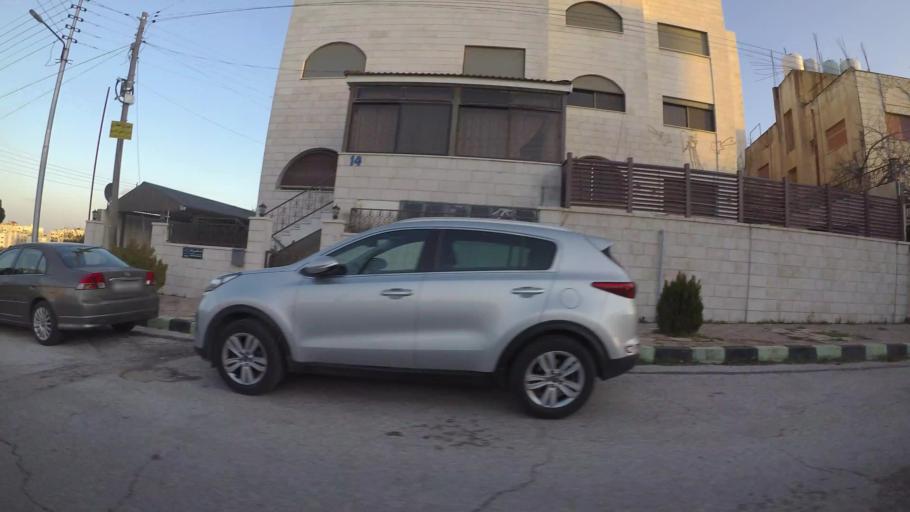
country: JO
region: Amman
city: Al Jubayhah
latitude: 31.9977
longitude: 35.8626
